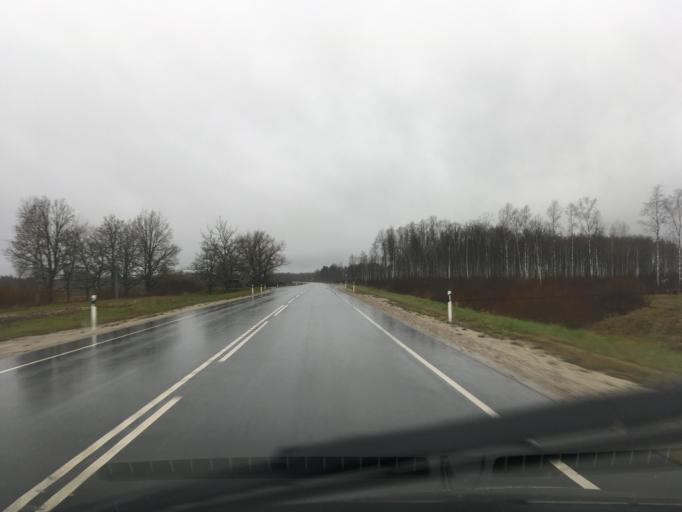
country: EE
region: Harju
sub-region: Nissi vald
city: Turba
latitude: 58.8588
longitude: 24.0729
